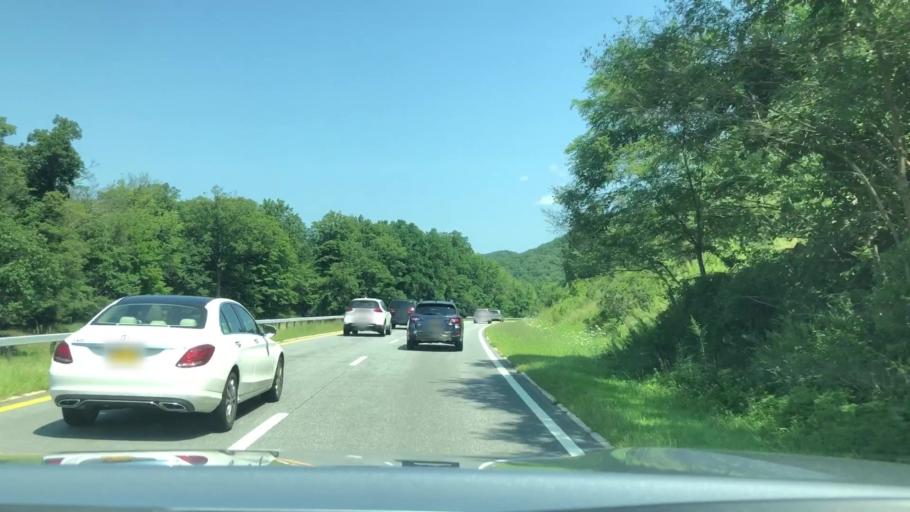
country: US
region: New York
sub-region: Orange County
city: Fort Montgomery
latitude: 41.3171
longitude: -74.0156
